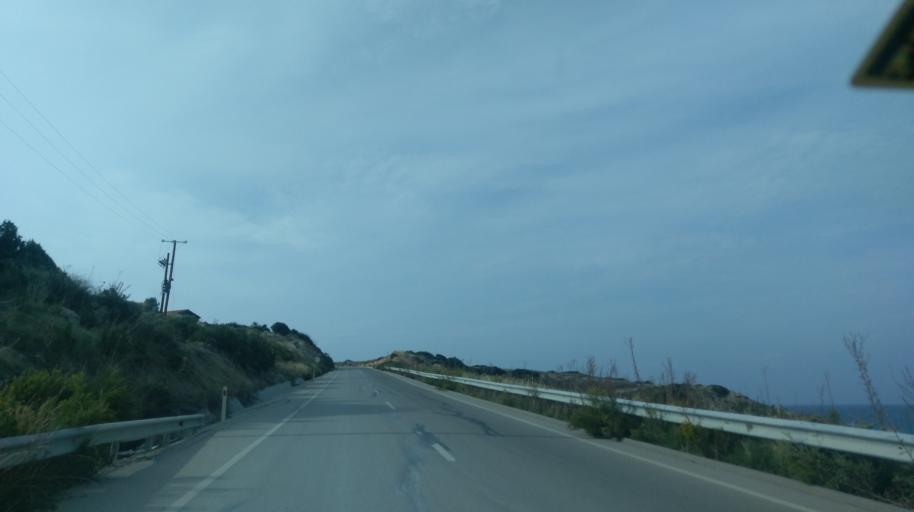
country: CY
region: Ammochostos
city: Trikomo
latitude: 35.4239
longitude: 33.8974
